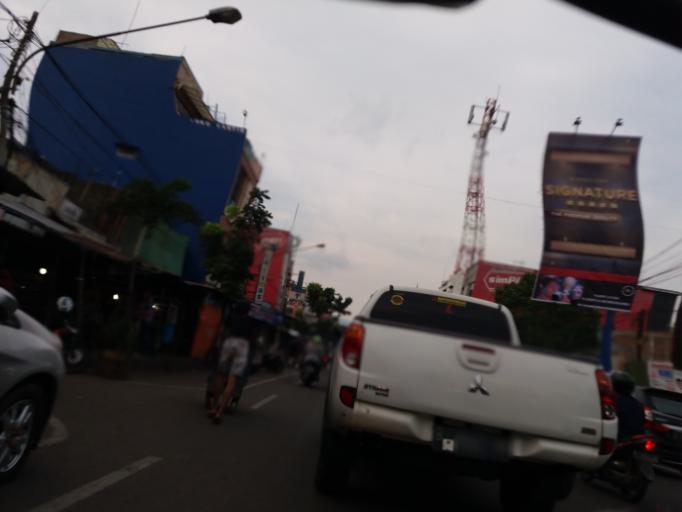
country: ID
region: West Java
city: Bandung
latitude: -6.9102
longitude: 107.6404
